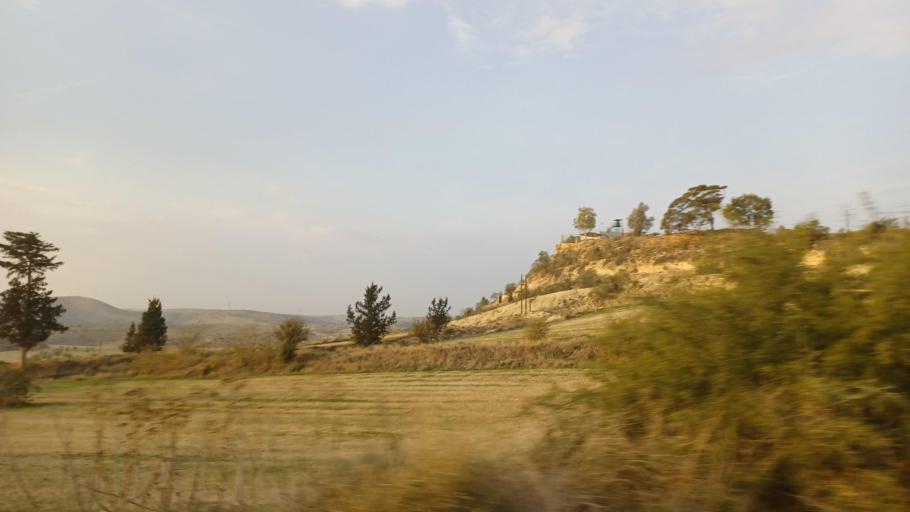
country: CY
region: Lefkosia
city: Lympia
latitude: 35.0055
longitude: 33.4979
